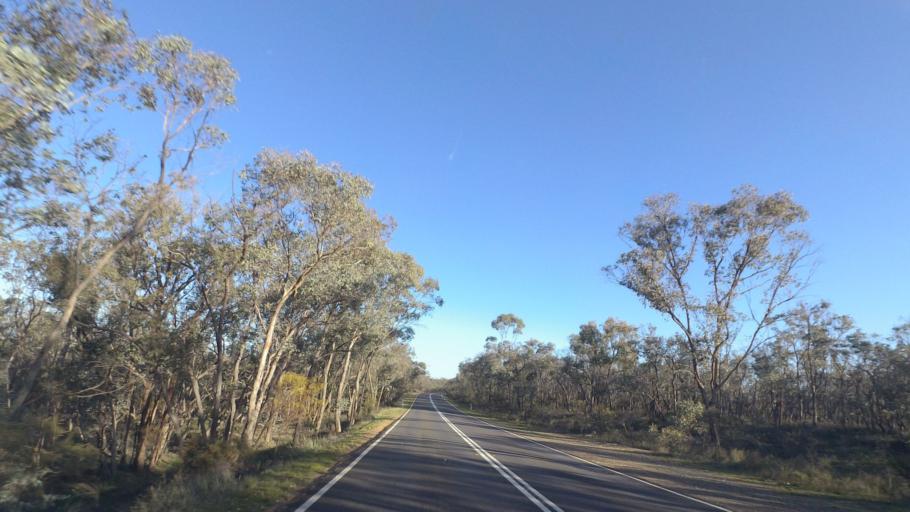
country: AU
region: Victoria
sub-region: Greater Bendigo
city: Kennington
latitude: -36.9277
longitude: 144.4891
